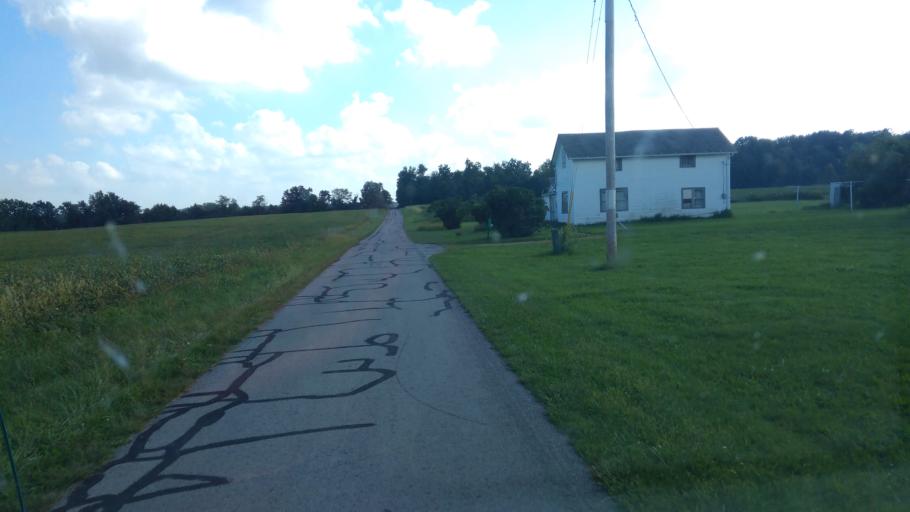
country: US
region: Ohio
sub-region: Hancock County
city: Arlington
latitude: 40.8447
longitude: -83.7085
